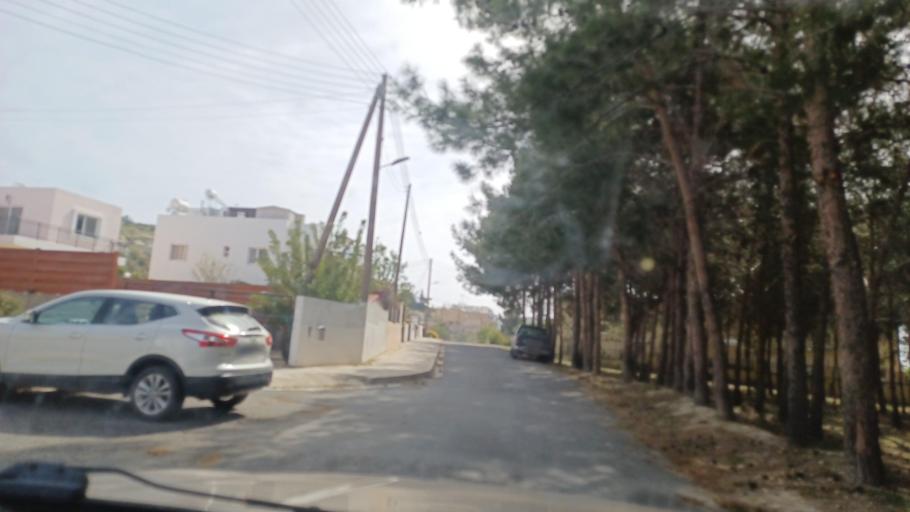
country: CY
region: Pafos
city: Paphos
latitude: 34.7613
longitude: 32.4722
